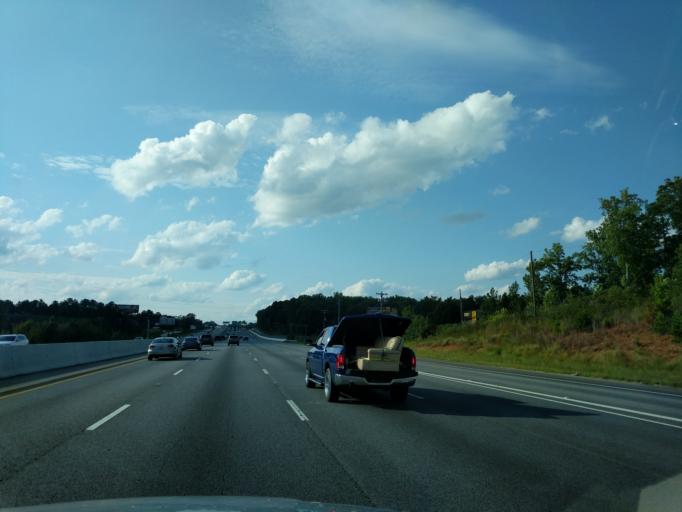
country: US
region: South Carolina
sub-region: Greenville County
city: Simpsonville
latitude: 34.7410
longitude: -82.2749
